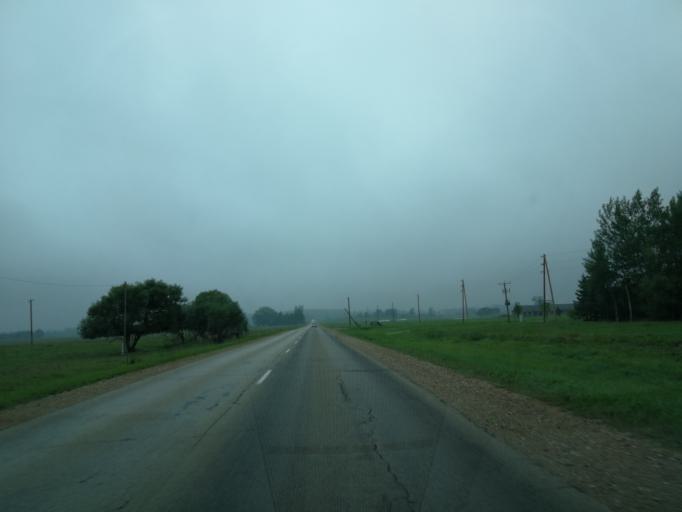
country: LV
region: Preilu Rajons
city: Preili
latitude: 56.2985
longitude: 26.6754
